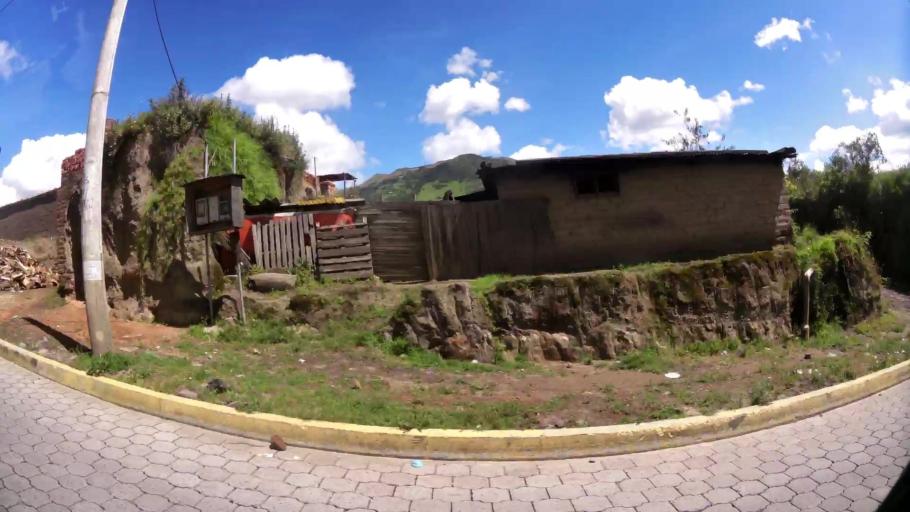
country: EC
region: Pichincha
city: Quito
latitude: -0.3257
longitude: -78.5664
